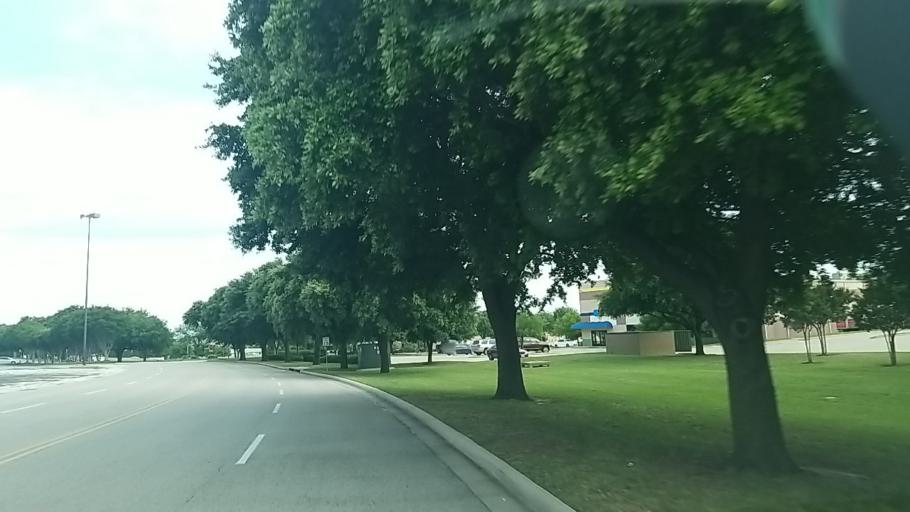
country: US
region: Texas
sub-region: Denton County
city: Lewisville
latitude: 33.0026
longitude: -96.9758
